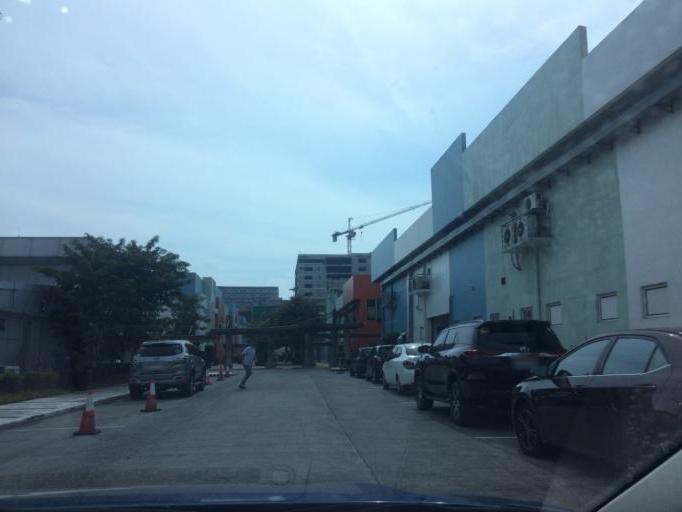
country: PH
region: Metro Manila
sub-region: Makati City
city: Makati City
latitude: 14.5376
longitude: 120.9906
